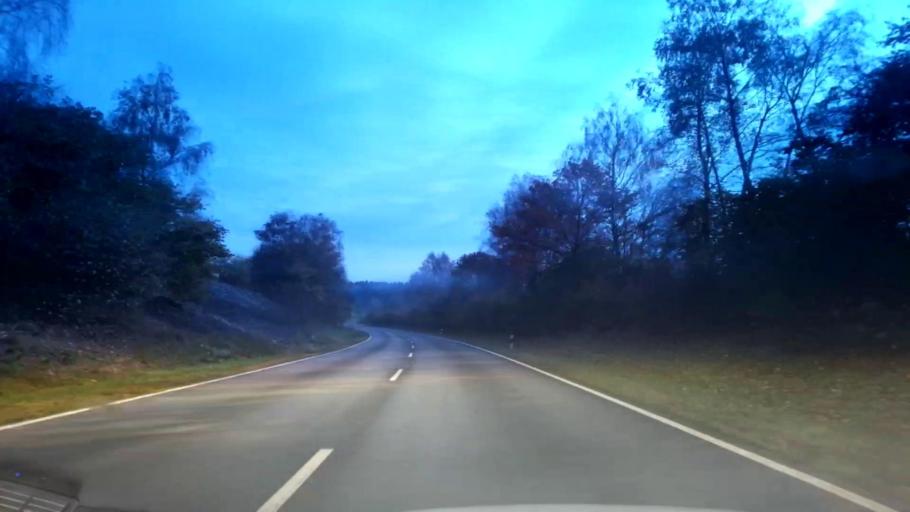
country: DE
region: Bavaria
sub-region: Upper Palatinate
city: Plossberg
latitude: 49.9154
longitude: 11.8255
